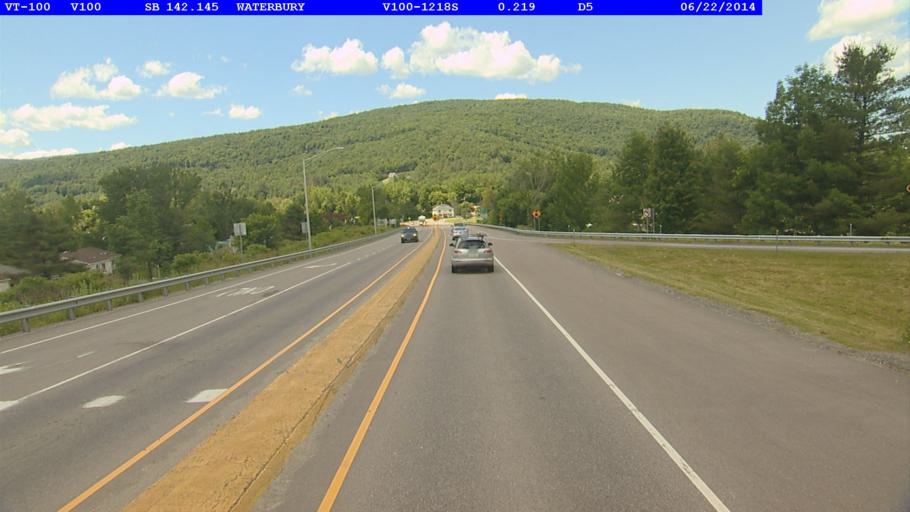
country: US
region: Vermont
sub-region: Washington County
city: Waterbury
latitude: 44.3426
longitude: -72.7557
